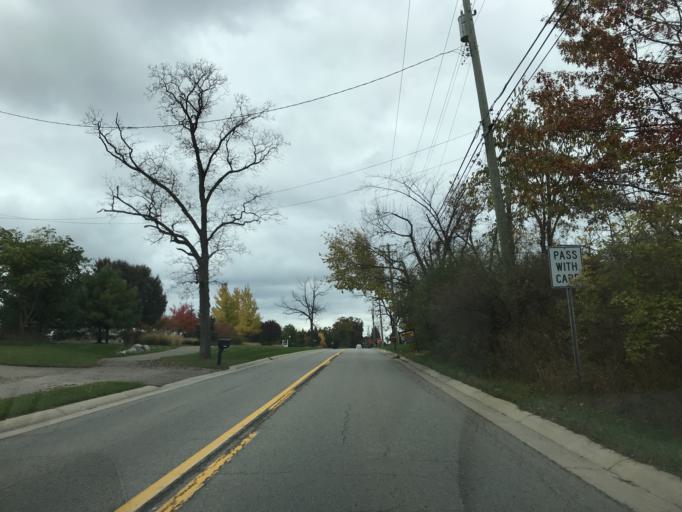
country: US
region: Michigan
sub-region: Oakland County
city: South Lyon
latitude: 42.4670
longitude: -83.6371
